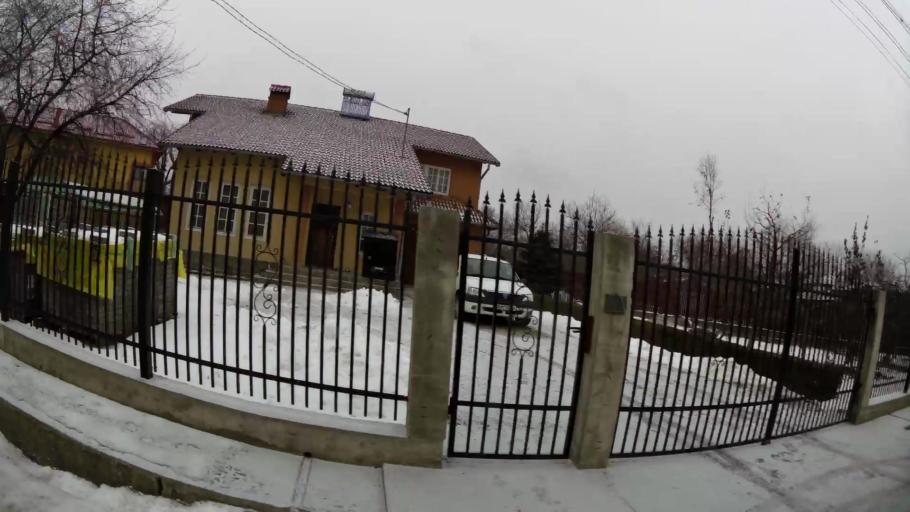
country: RO
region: Dambovita
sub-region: Municipiul Targoviste
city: Targoviste
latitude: 44.9395
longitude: 25.4747
